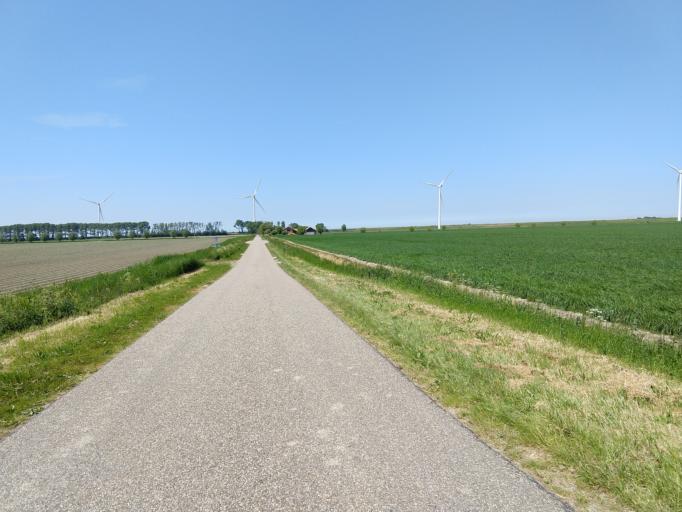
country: NL
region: Zeeland
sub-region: Schouwen-Duiveland
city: Bruinisse
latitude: 51.6019
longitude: 4.0704
